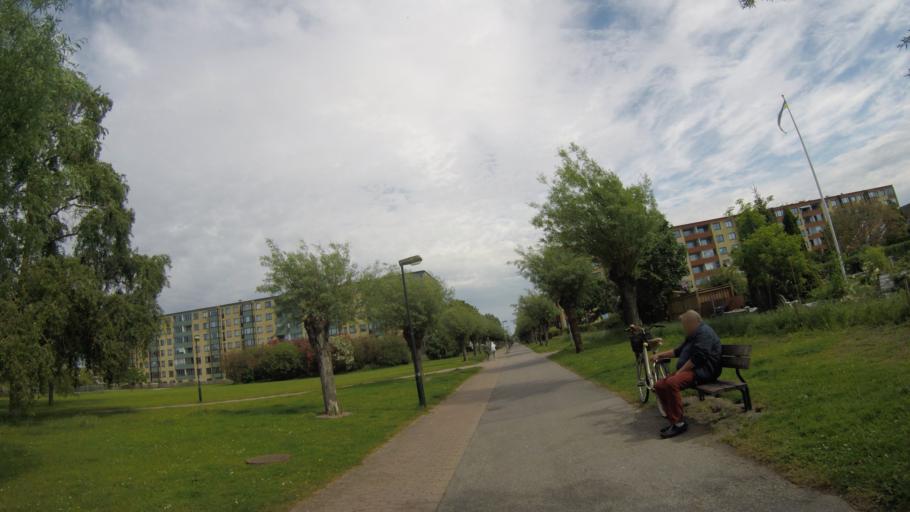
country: SE
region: Skane
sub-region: Malmo
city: Malmoe
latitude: 55.5827
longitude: 12.9732
